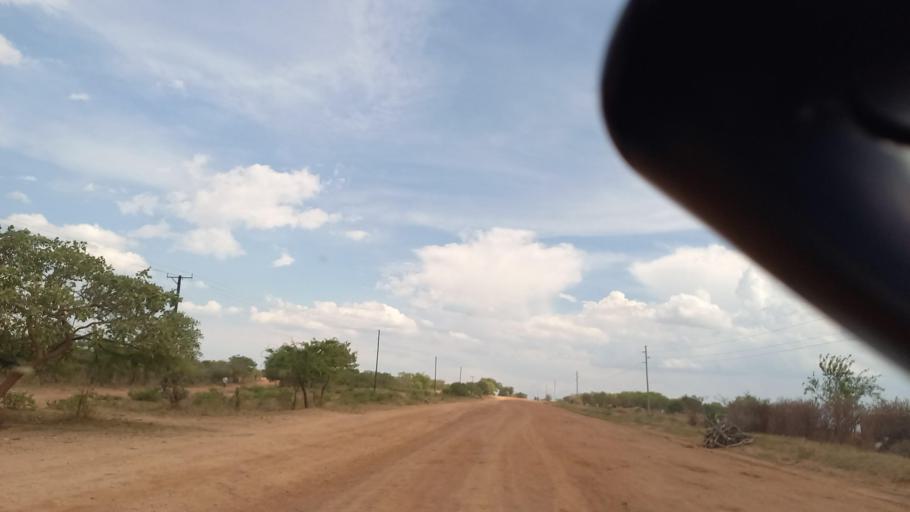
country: ZM
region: Lusaka
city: Kafue
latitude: -16.1434
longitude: 28.0546
